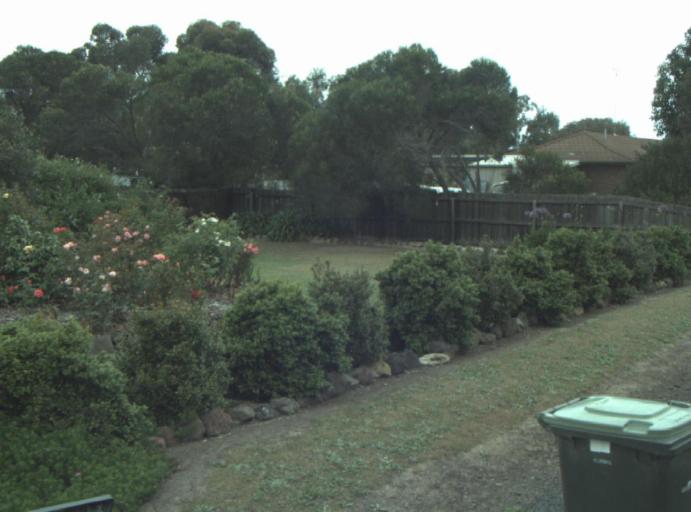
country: AU
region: Victoria
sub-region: Greater Geelong
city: East Geelong
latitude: -38.1698
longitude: 144.4141
